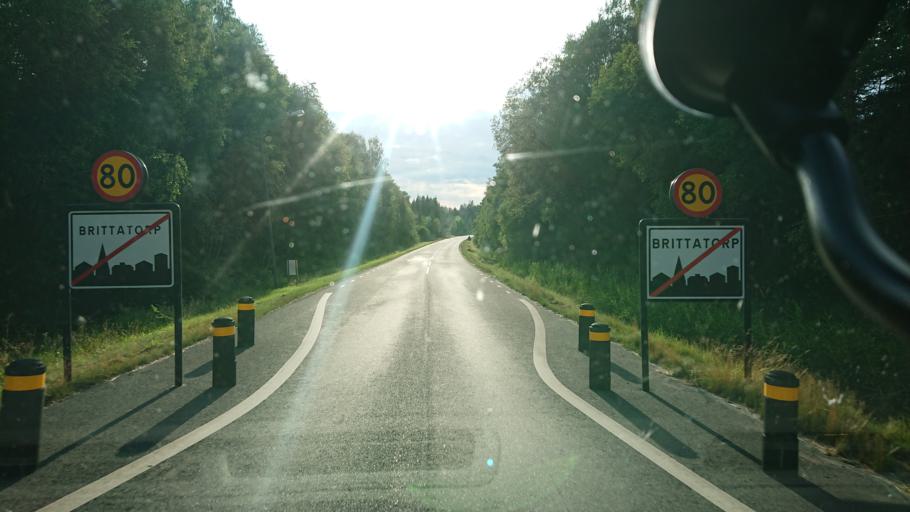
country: SE
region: Kronoberg
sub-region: Vaxjo Kommun
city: Rottne
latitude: 57.0341
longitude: 14.9323
